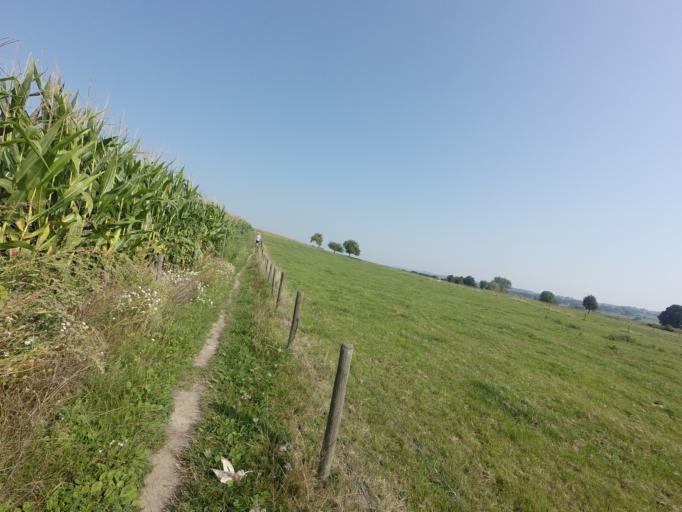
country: BE
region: Wallonia
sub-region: Province de Liege
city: Plombieres
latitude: 50.7794
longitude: 5.9119
